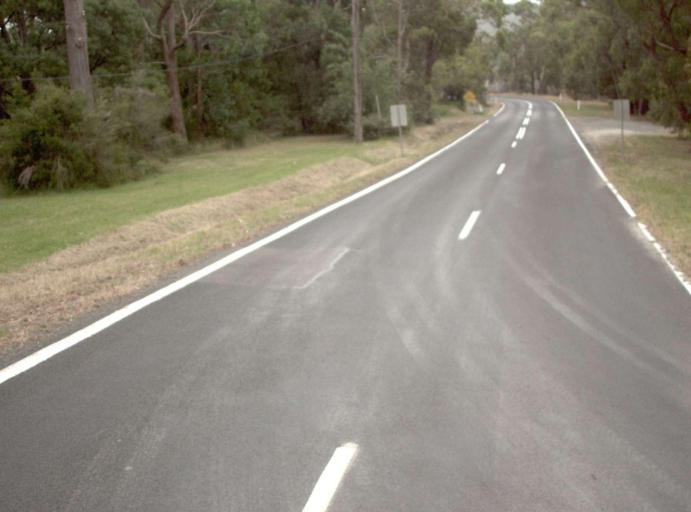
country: AU
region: Victoria
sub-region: Yarra Ranges
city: Badger Creek
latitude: -37.6908
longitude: 145.5471
